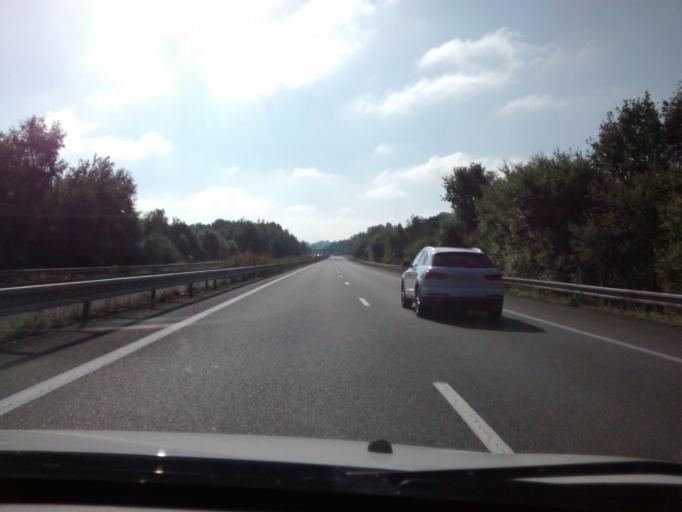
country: FR
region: Pays de la Loire
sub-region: Departement de la Mayenne
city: Loiron
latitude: 48.0768
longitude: -0.9614
